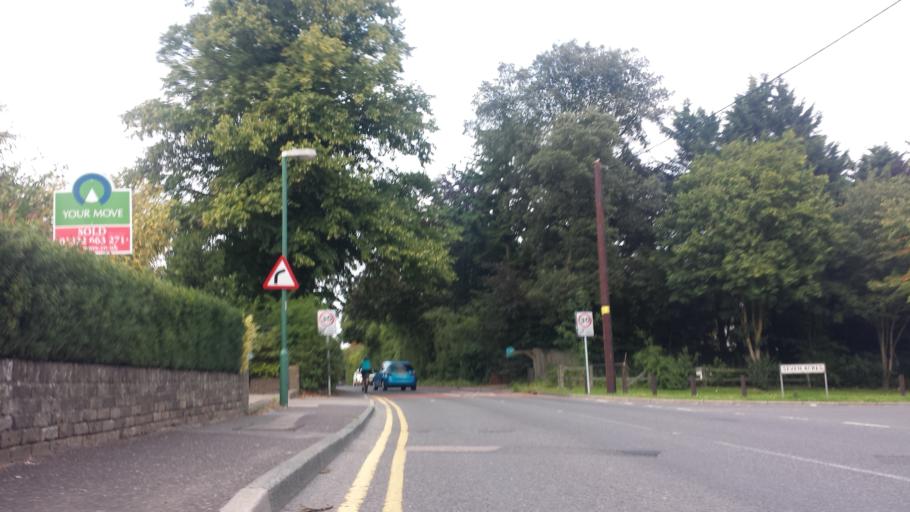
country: GB
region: England
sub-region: Kent
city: Swanley
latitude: 51.3849
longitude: 0.1621
